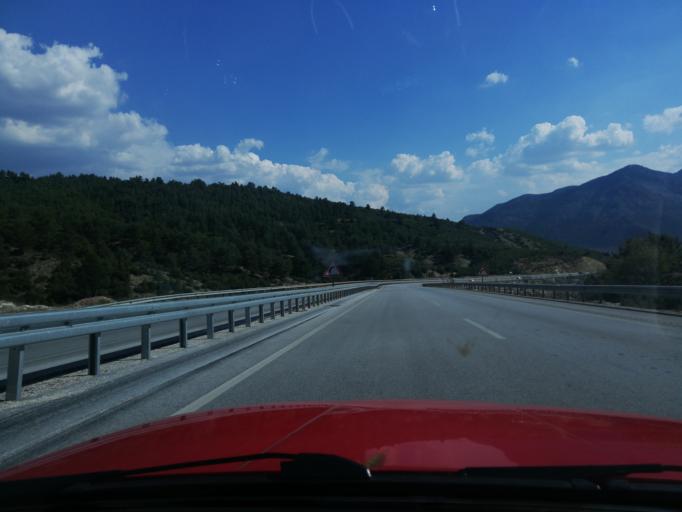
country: TR
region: Burdur
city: Celtikci
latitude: 37.5741
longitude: 30.4500
